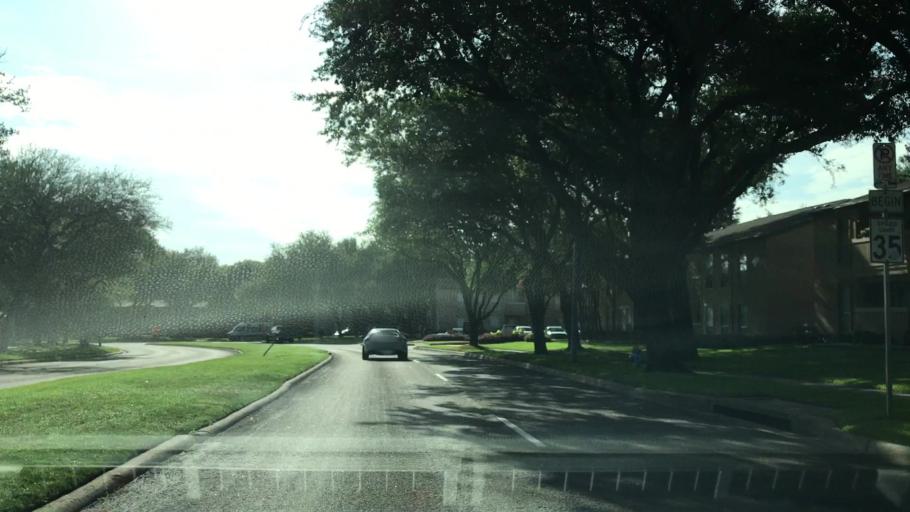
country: US
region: Texas
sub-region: Dallas County
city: University Park
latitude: 32.8571
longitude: -96.7672
